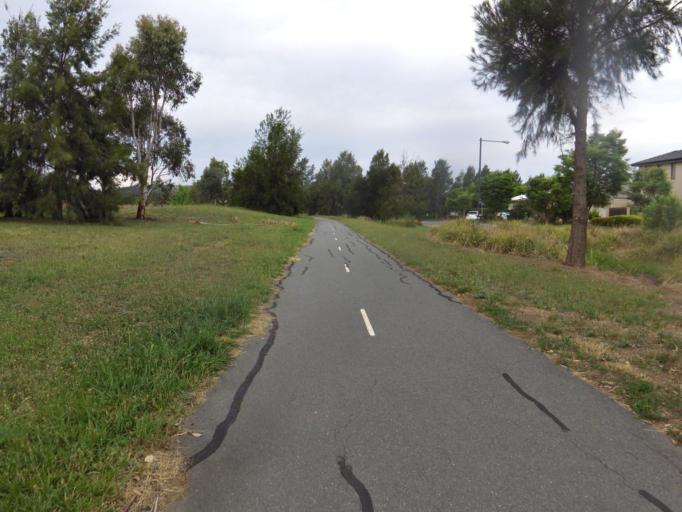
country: AU
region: Australian Capital Territory
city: Kaleen
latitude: -35.1680
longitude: 149.1407
